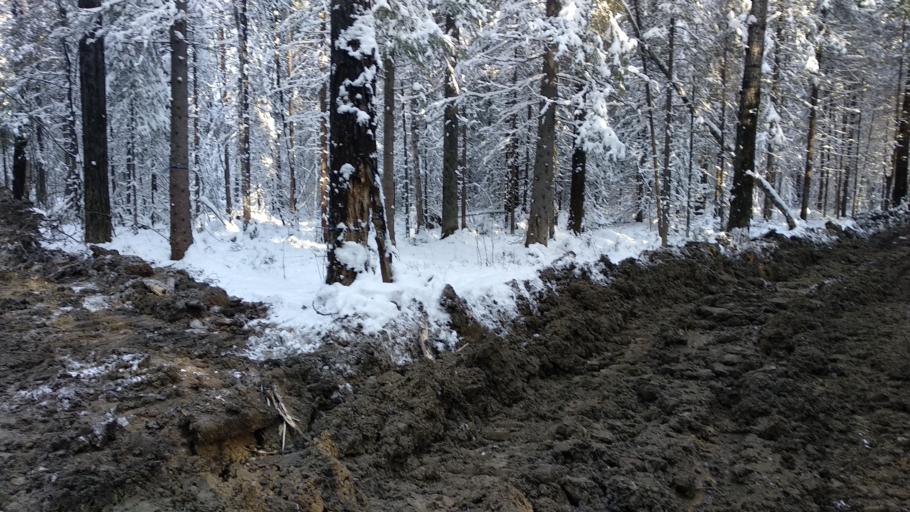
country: RU
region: Sverdlovsk
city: Krasnotur'insk
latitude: 59.7299
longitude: 60.1537
